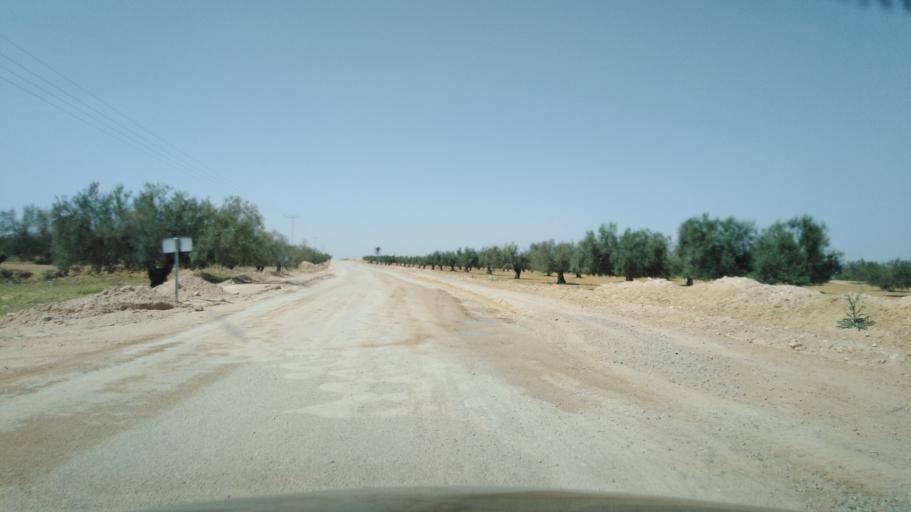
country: TN
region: Safaqis
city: Sfax
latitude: 34.6869
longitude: 10.4632
